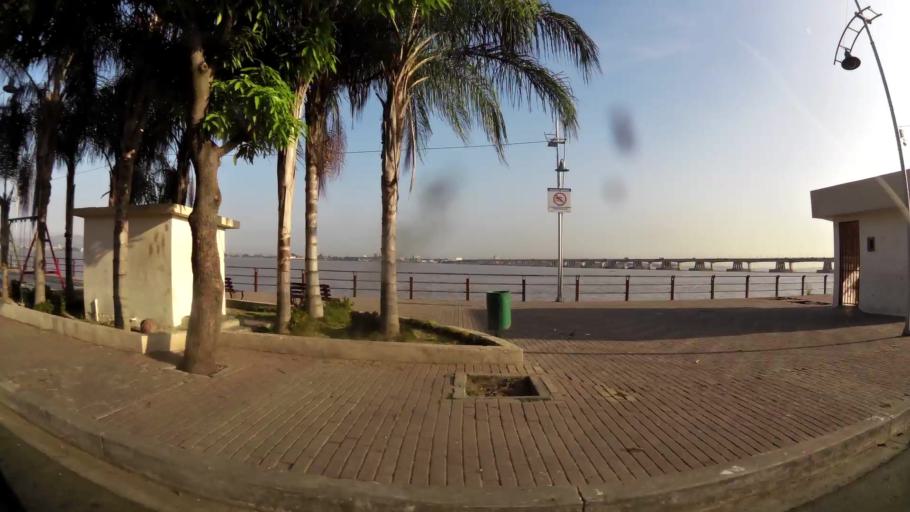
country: EC
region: Guayas
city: Eloy Alfaro
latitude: -2.1672
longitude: -79.8506
